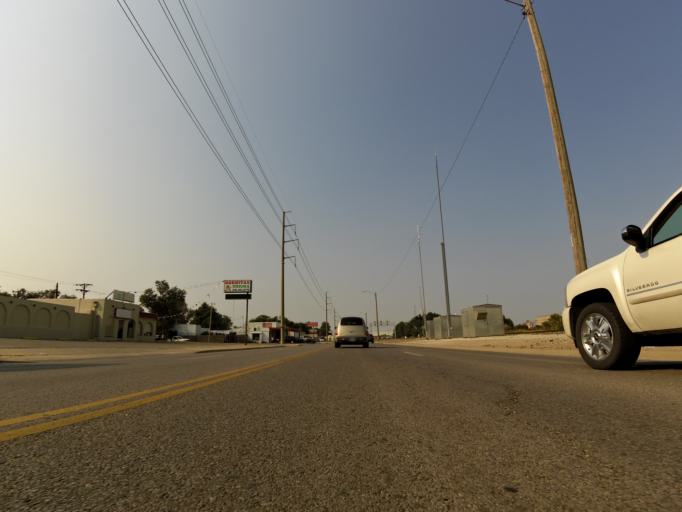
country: US
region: Kansas
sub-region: Sedgwick County
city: Wichita
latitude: 37.7256
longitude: -97.3359
